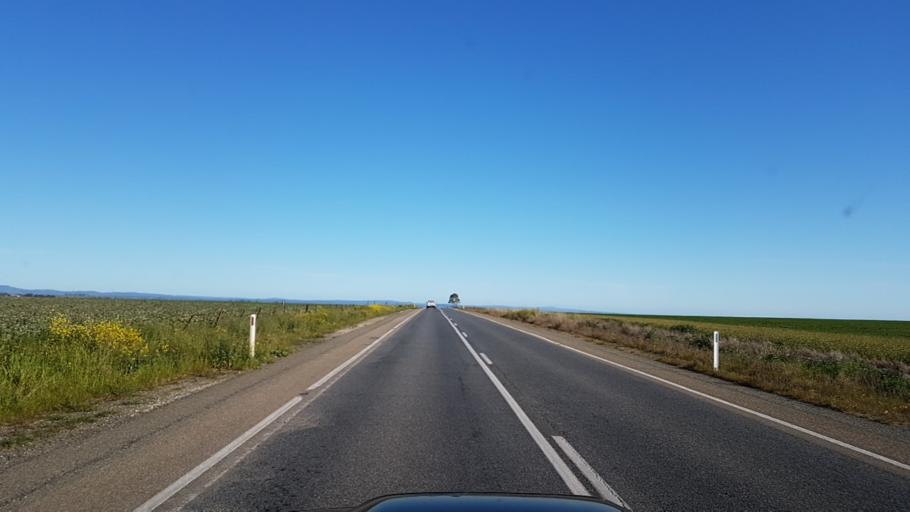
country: AU
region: South Australia
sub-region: Light
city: Freeling
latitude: -34.4521
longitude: 138.7450
